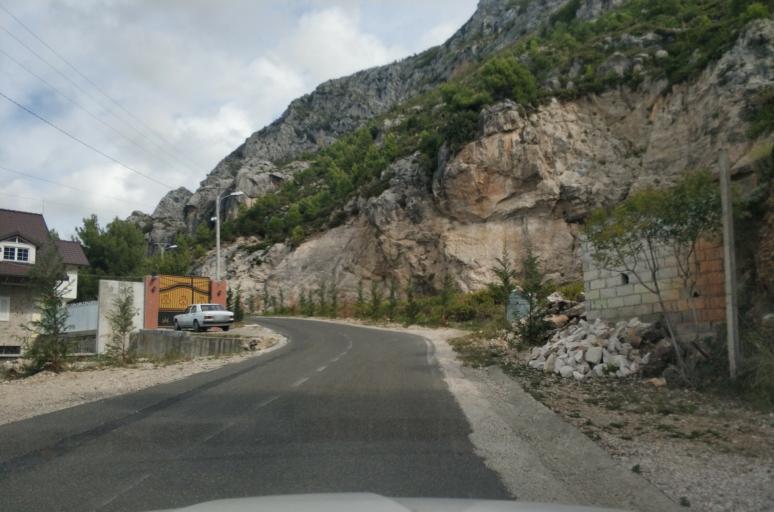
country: AL
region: Durres
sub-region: Rrethi i Krujes
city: Kruje
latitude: 41.5171
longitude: 19.7942
